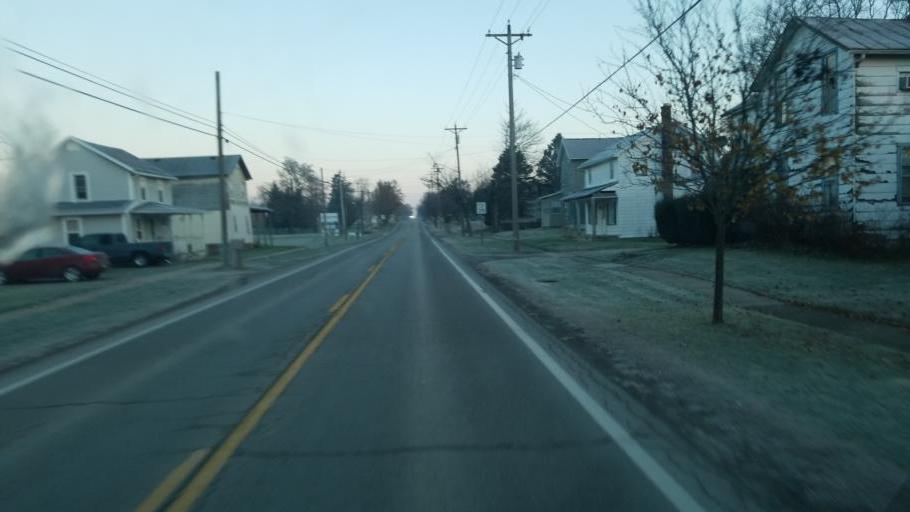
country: US
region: Ohio
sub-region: Wayne County
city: West Salem
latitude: 40.9676
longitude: -82.1096
